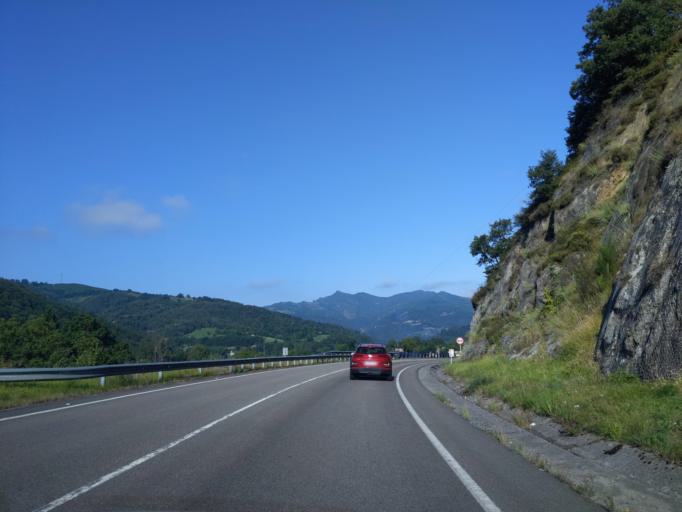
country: ES
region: Asturias
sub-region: Province of Asturias
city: Pola de Laviana
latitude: 43.2342
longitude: -5.5186
